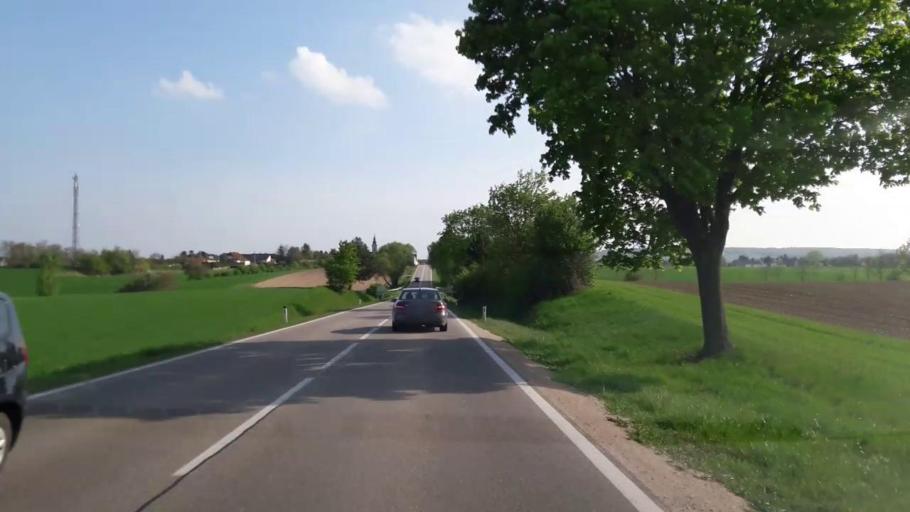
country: AT
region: Lower Austria
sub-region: Politischer Bezirk Hollabrunn
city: Wullersdorf
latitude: 48.6089
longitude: 16.0656
